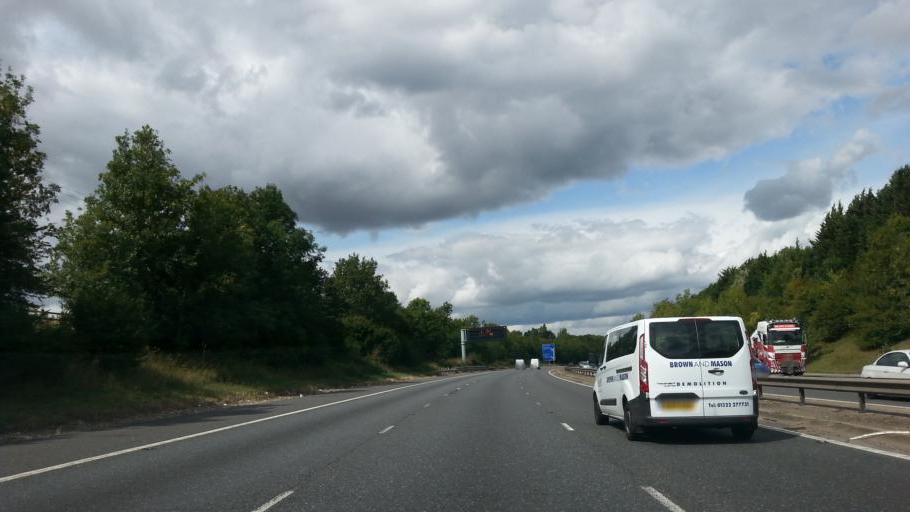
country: GB
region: England
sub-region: Essex
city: Little Hallingbury
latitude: 51.8444
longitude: 0.1881
